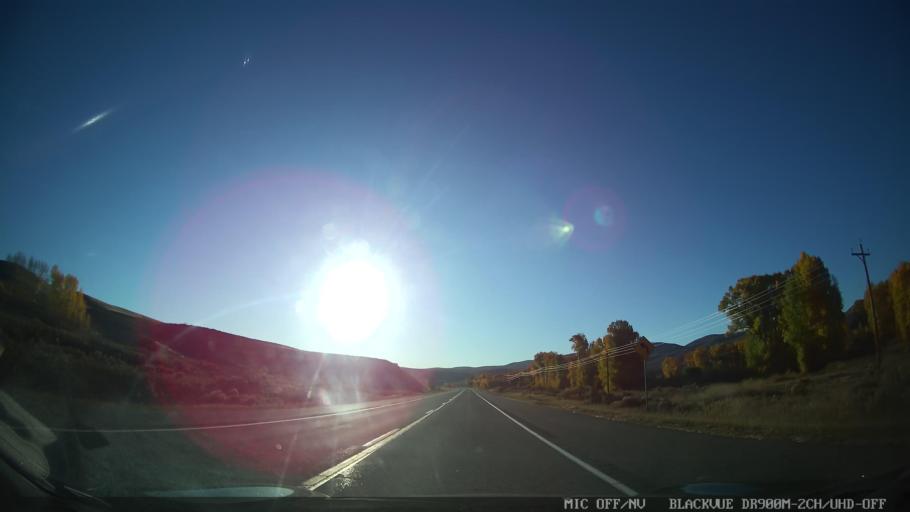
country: US
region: Colorado
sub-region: Grand County
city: Kremmling
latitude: 40.0650
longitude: -106.2545
